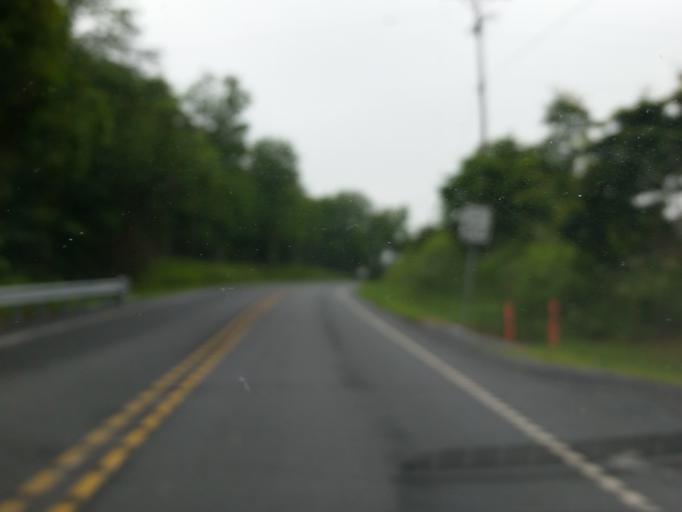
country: US
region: Pennsylvania
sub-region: Schuylkill County
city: Tower City
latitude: 40.5205
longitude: -76.4976
